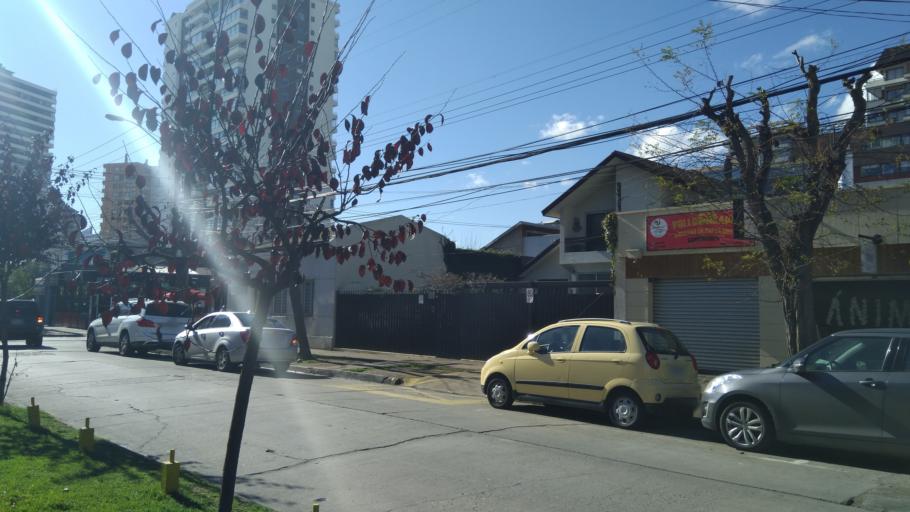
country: CL
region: Valparaiso
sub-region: Provincia de Valparaiso
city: Vina del Mar
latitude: -33.0170
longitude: -71.5555
